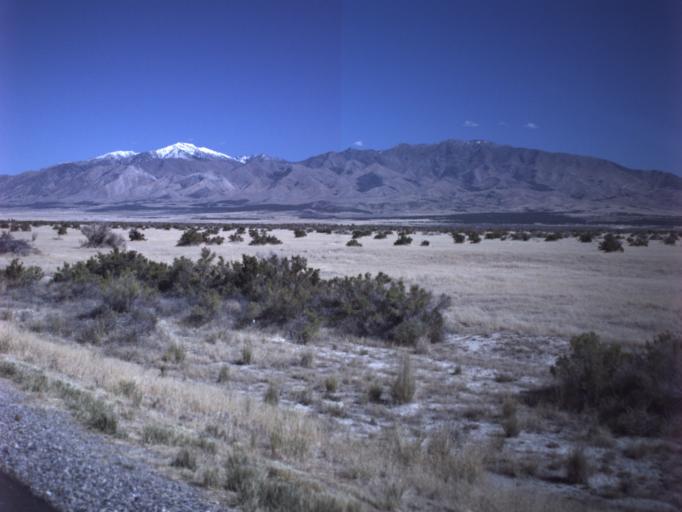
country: US
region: Utah
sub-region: Tooele County
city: Grantsville
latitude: 40.2724
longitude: -112.7414
